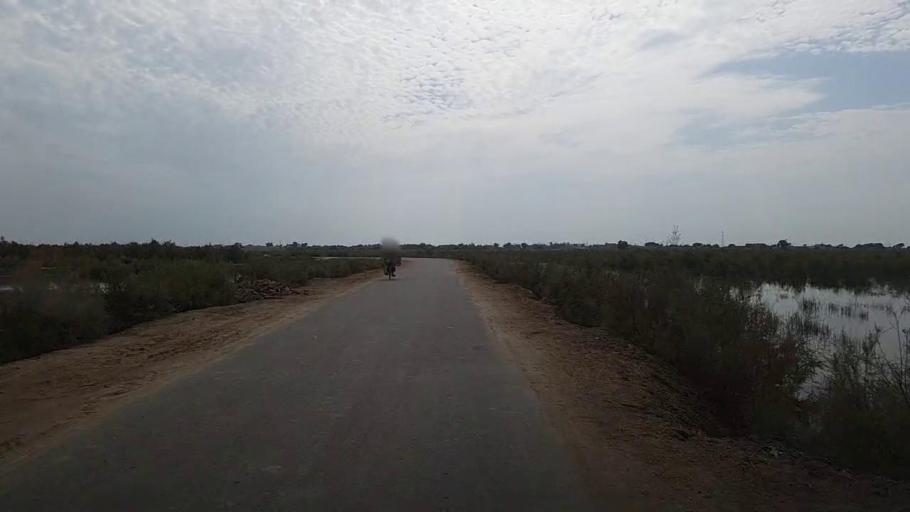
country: PK
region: Sindh
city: Thul
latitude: 28.2646
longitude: 68.7796
